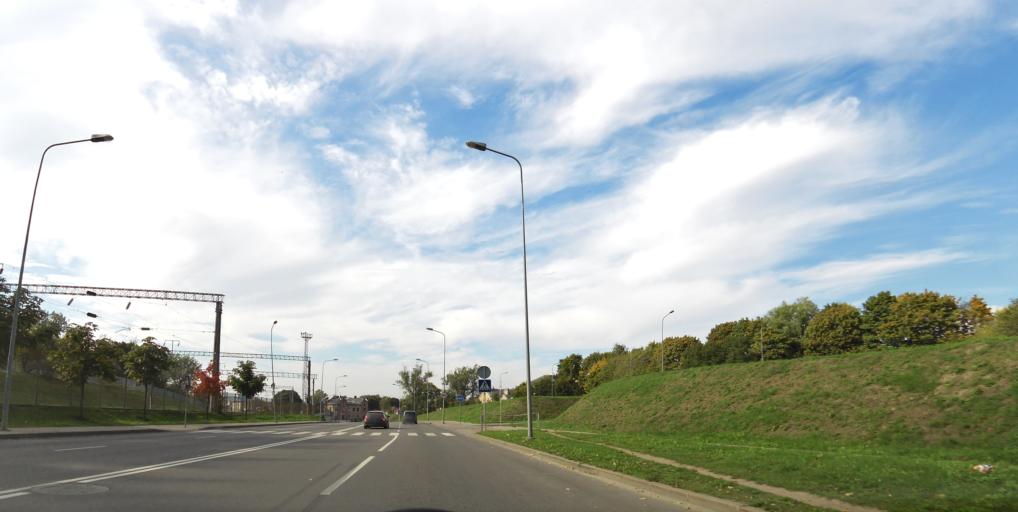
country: LT
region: Vilnius County
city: Rasos
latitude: 54.6729
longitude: 25.2946
